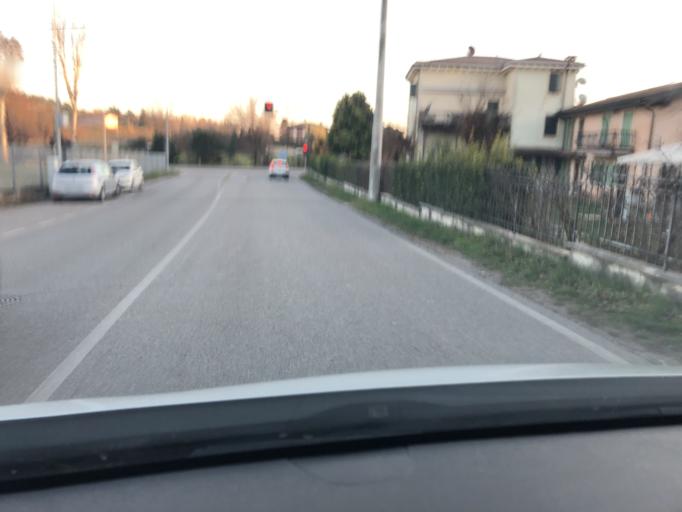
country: IT
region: Veneto
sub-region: Provincia di Verona
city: Sona
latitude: 45.4443
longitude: 10.8212
